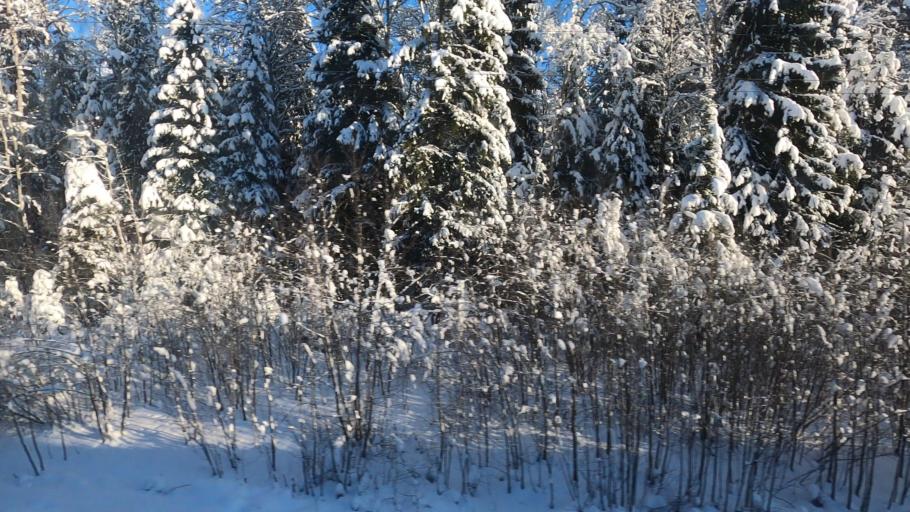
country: RU
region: Moskovskaya
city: Novo-Nikol'skoye
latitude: 56.6170
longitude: 37.5663
